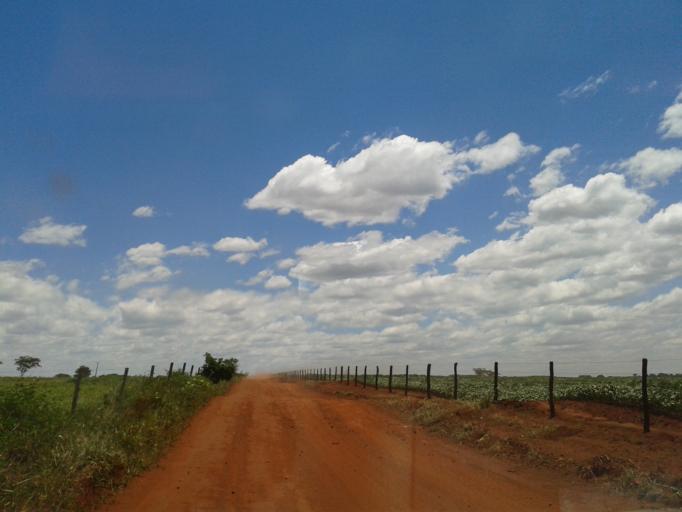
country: BR
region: Minas Gerais
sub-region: Centralina
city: Centralina
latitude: -18.7138
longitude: -49.2144
